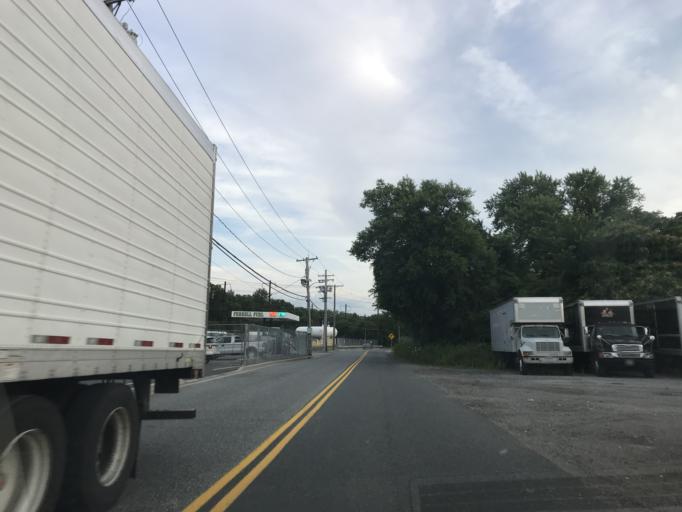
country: US
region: Maryland
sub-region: Harford County
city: Aberdeen
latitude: 39.4986
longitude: -76.1699
